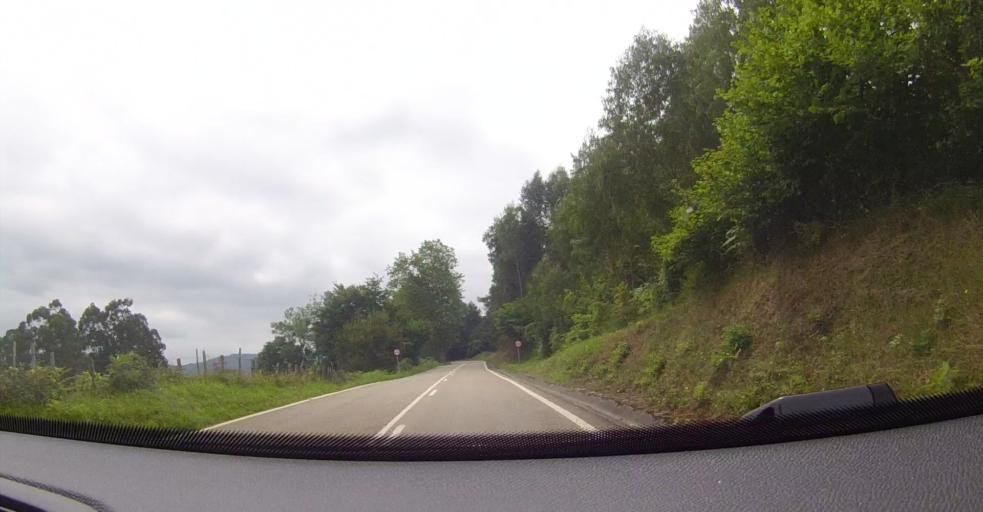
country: ES
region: Basque Country
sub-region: Bizkaia
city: Balmaseda
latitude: 43.2406
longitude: -3.2877
